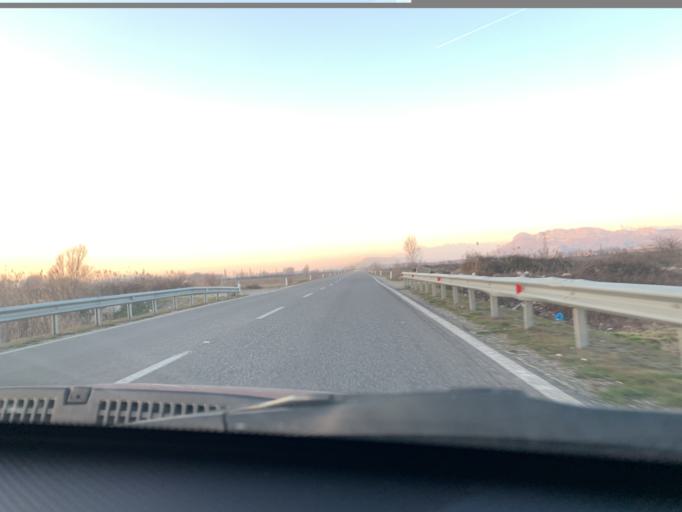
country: AL
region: Lezhe
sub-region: Rrethi i Lezhes
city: Balldreni i Ri
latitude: 41.8442
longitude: 19.6433
